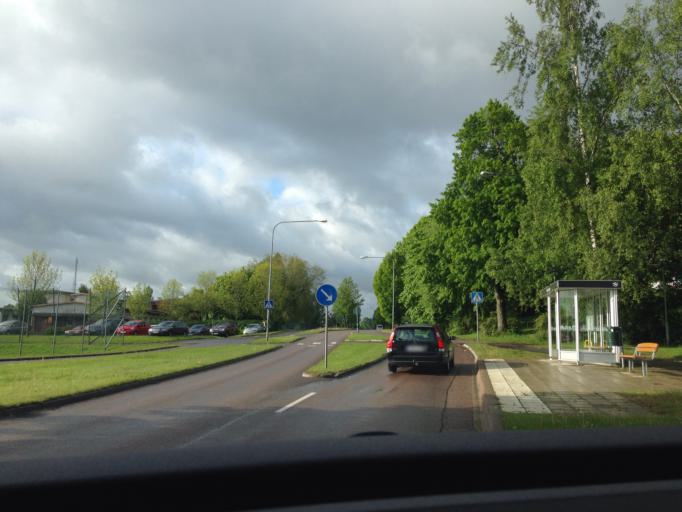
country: SE
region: Vaestra Goetaland
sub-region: Skovde Kommun
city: Skoevde
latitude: 58.4111
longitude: 13.8658
